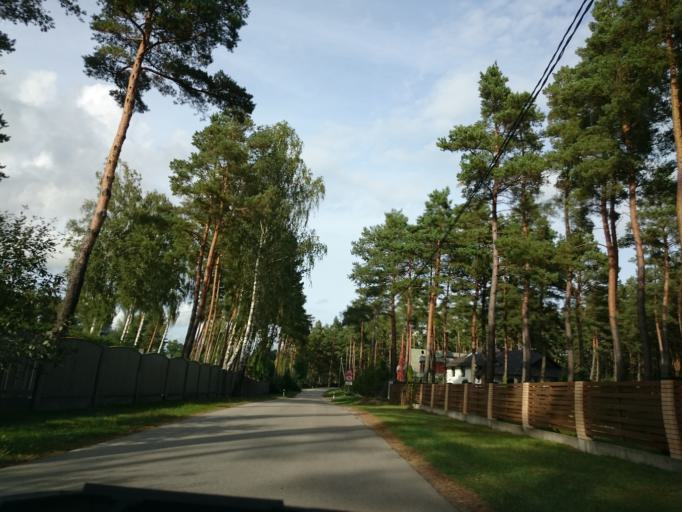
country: LV
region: Adazi
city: Adazi
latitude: 57.0396
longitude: 24.3326
